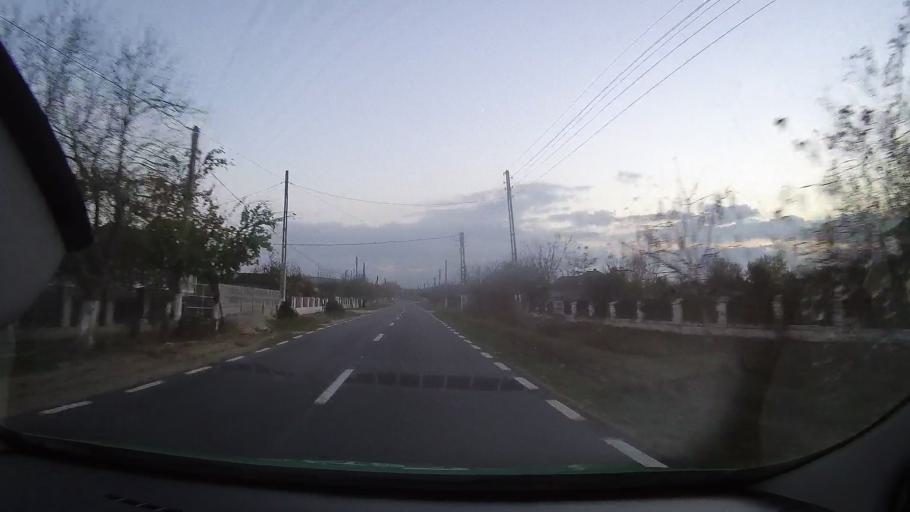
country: RO
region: Constanta
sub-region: Comuna Oltina
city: Oltina
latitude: 44.1594
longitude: 27.6676
